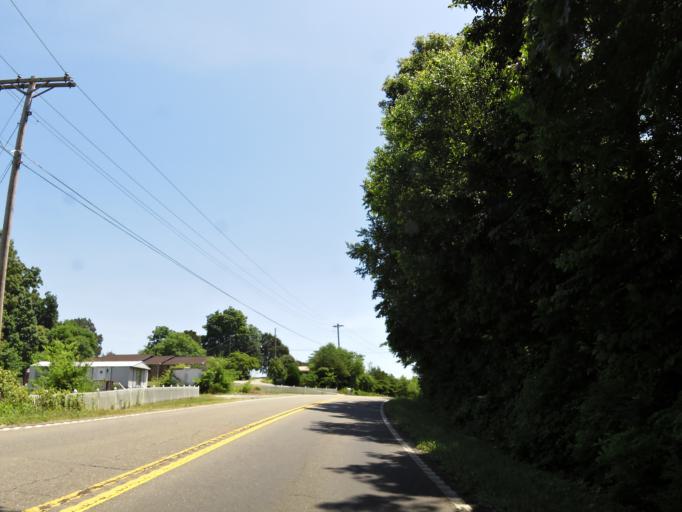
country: US
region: Tennessee
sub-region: Jefferson County
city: Dandridge
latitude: 36.0246
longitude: -83.4632
